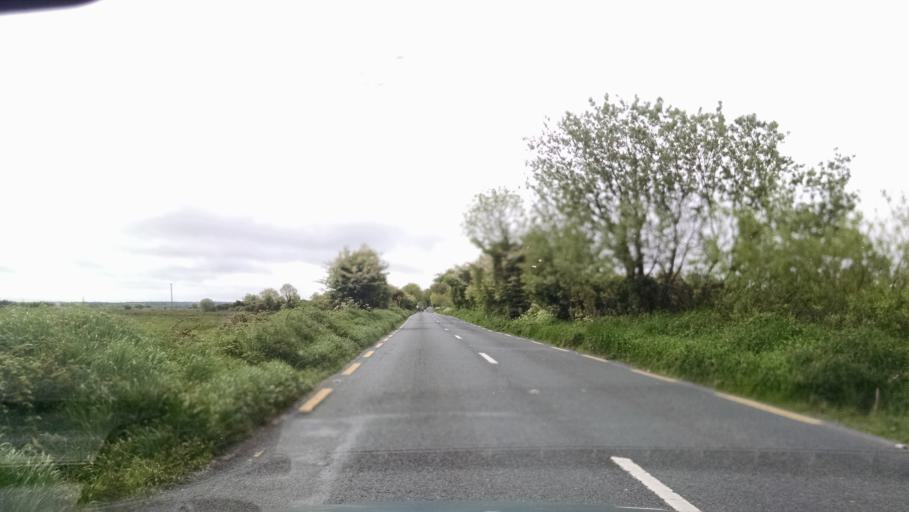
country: IE
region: Connaught
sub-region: County Galway
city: Claregalway
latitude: 53.3676
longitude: -9.0169
